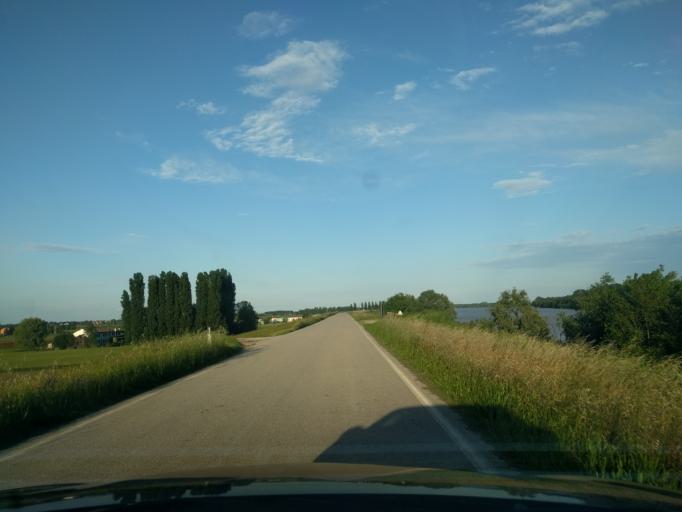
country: IT
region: Veneto
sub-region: Provincia di Rovigo
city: Guarda Veneta
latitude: 44.9799
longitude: 11.8099
